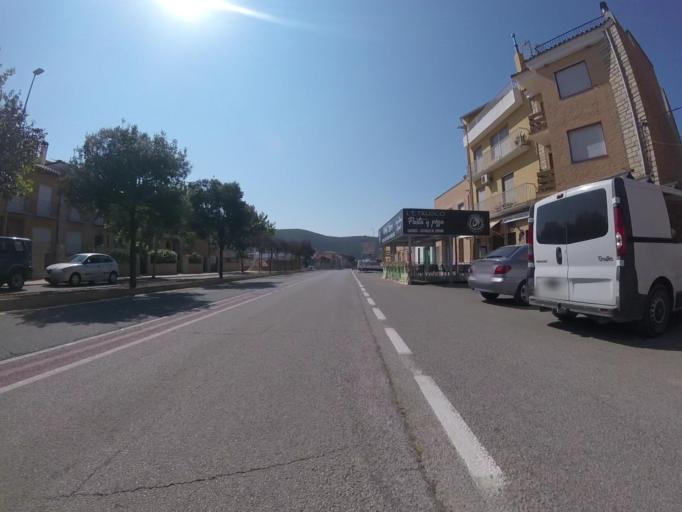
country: ES
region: Valencia
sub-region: Provincia de Castello
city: Adzaneta
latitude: 40.2203
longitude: -0.1712
